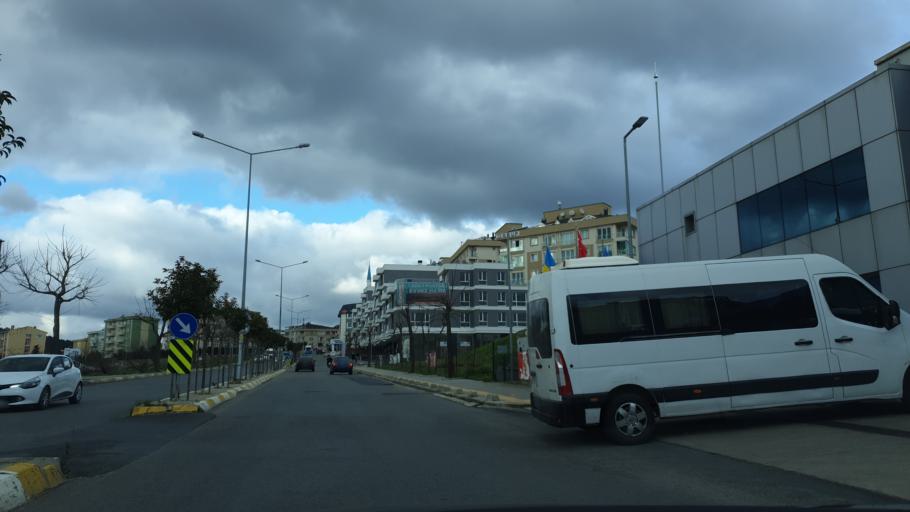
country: TR
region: Istanbul
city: Pendik
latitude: 40.9017
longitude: 29.2469
